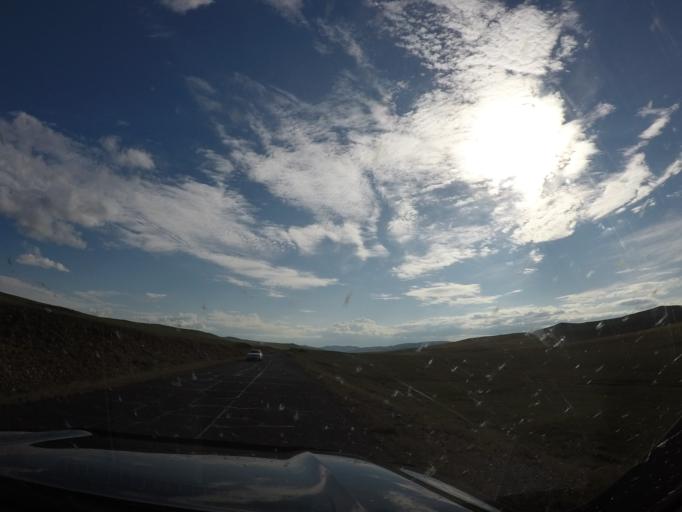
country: MN
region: Hentiy
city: Modot
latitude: 47.7841
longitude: 108.6663
